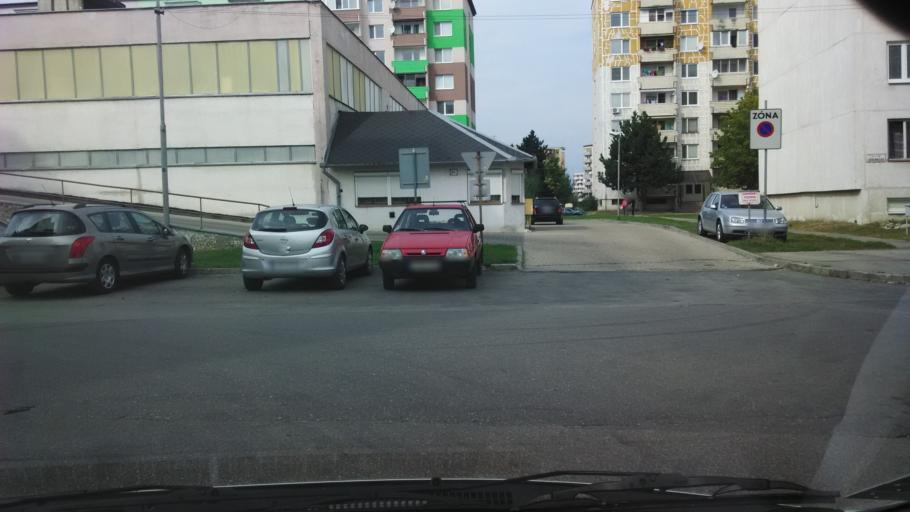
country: SK
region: Nitriansky
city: Levice
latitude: 48.2052
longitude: 18.6043
